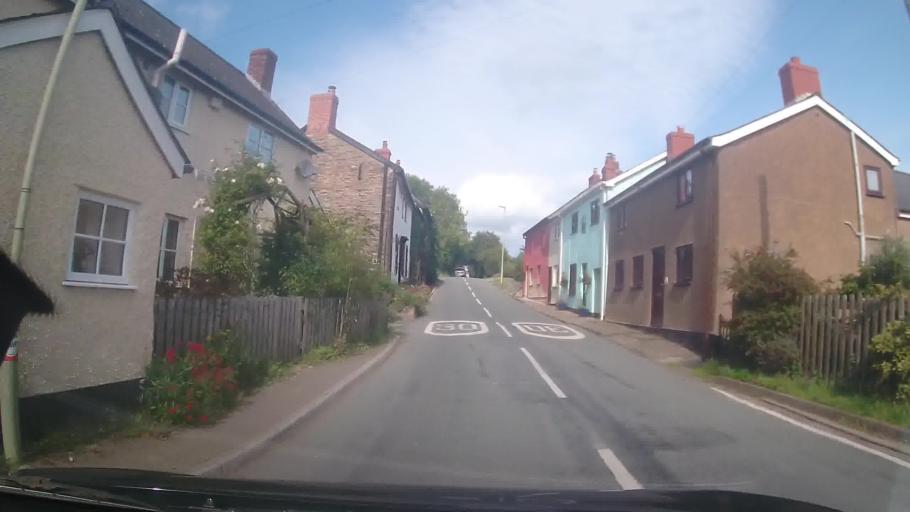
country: GB
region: England
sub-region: Shropshire
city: Bishop's Castle
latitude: 52.4961
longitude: -2.9979
